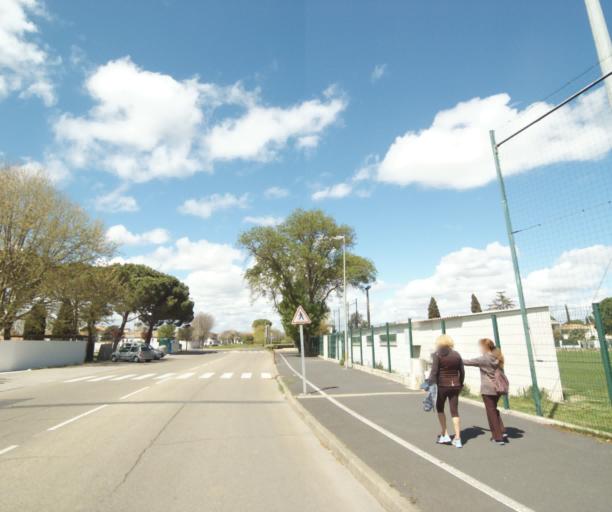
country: FR
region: Languedoc-Roussillon
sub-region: Departement de l'Herault
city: Lattes
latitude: 43.5674
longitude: 3.9072
